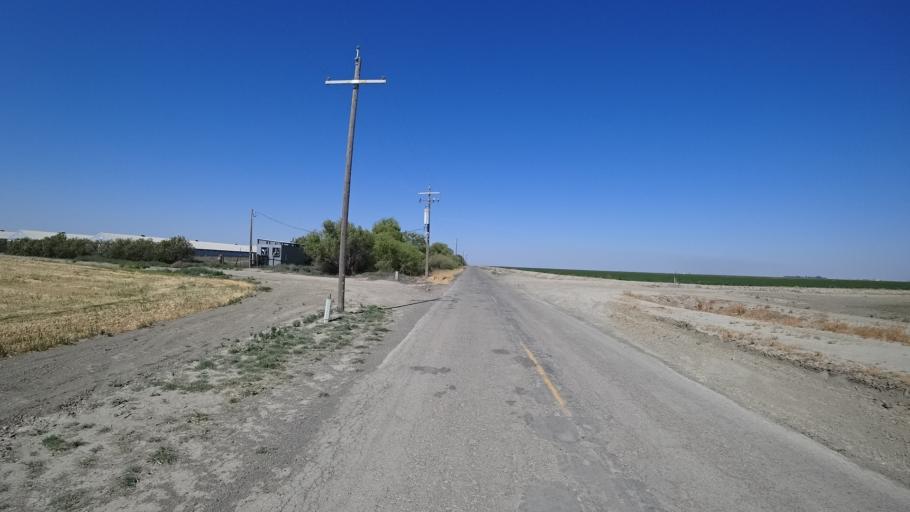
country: US
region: California
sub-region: Kings County
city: Corcoran
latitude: 36.0072
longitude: -119.5448
